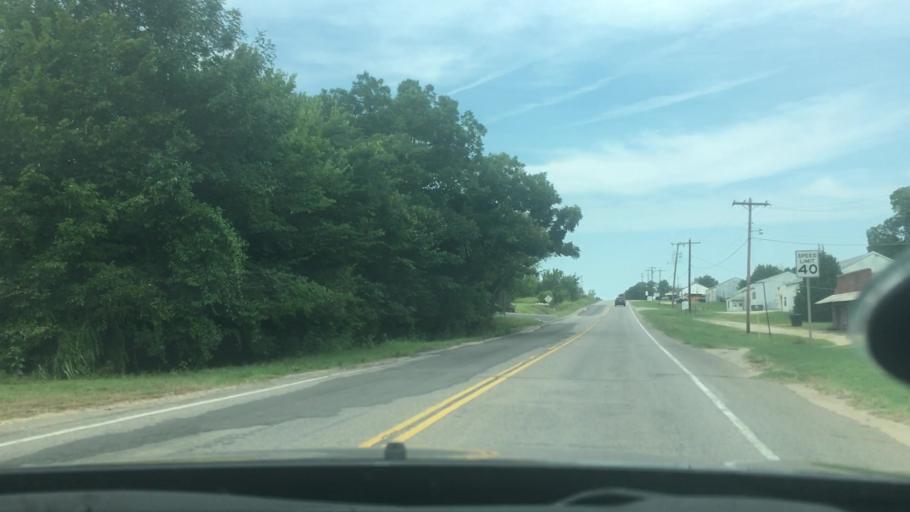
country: US
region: Oklahoma
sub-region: Seminole County
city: Seminole
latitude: 35.2253
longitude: -96.6797
